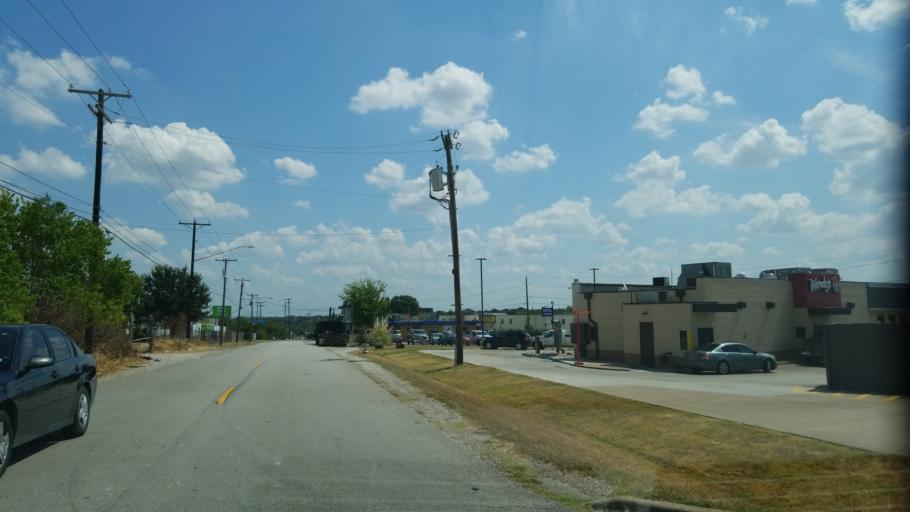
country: US
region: Texas
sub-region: Dallas County
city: Cockrell Hill
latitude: 32.7641
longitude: -96.8544
